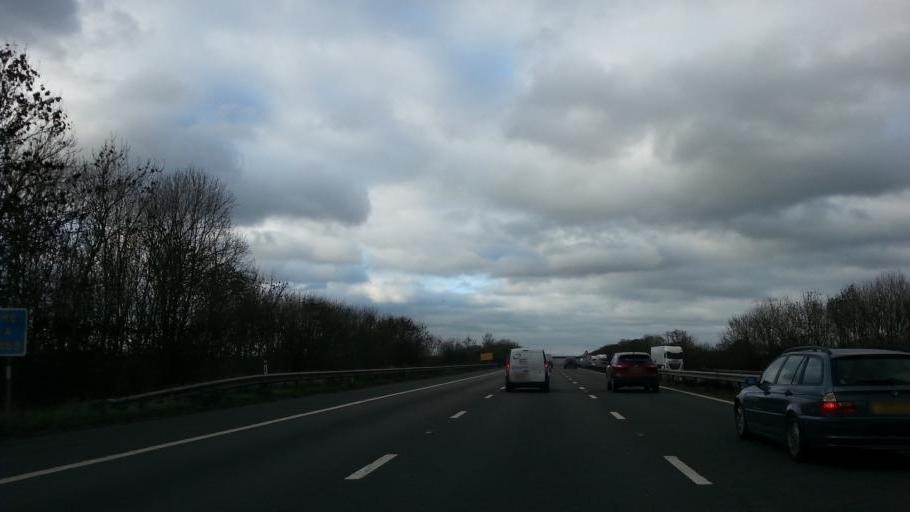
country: GB
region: England
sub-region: Warwickshire
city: Brandon
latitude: 52.4349
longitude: -1.3563
